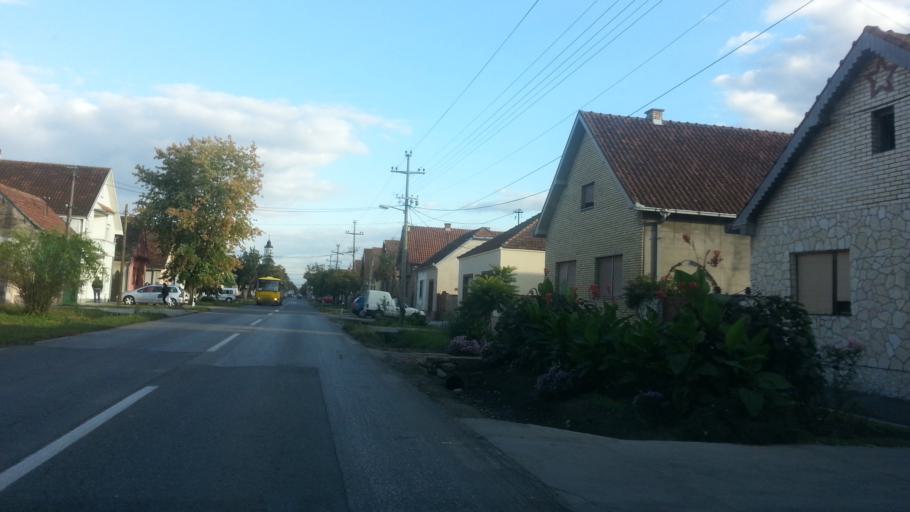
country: RS
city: Novi Banovci
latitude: 44.9086
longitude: 20.2705
